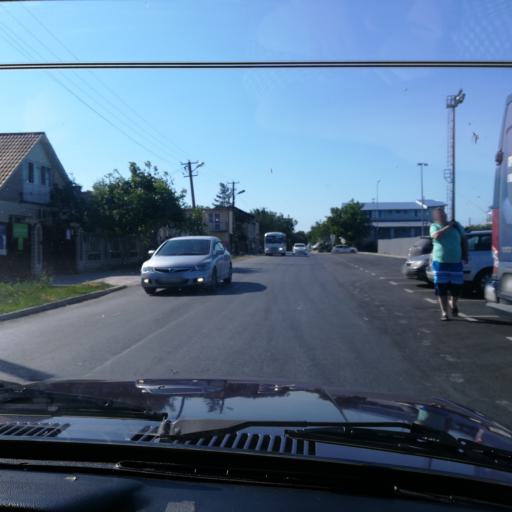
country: RU
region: Krasnodarskiy
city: Vityazevo
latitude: 45.0041
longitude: 37.2857
